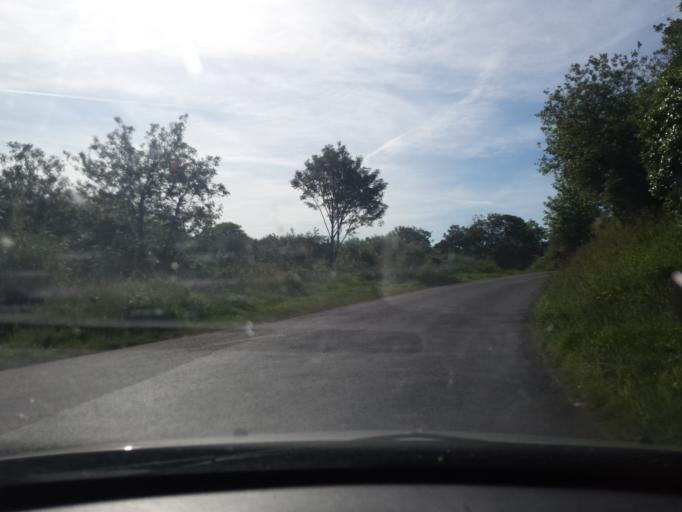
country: FR
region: Lower Normandy
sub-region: Departement de la Manche
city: Beaumont-Hague
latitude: 49.6852
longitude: -1.9237
